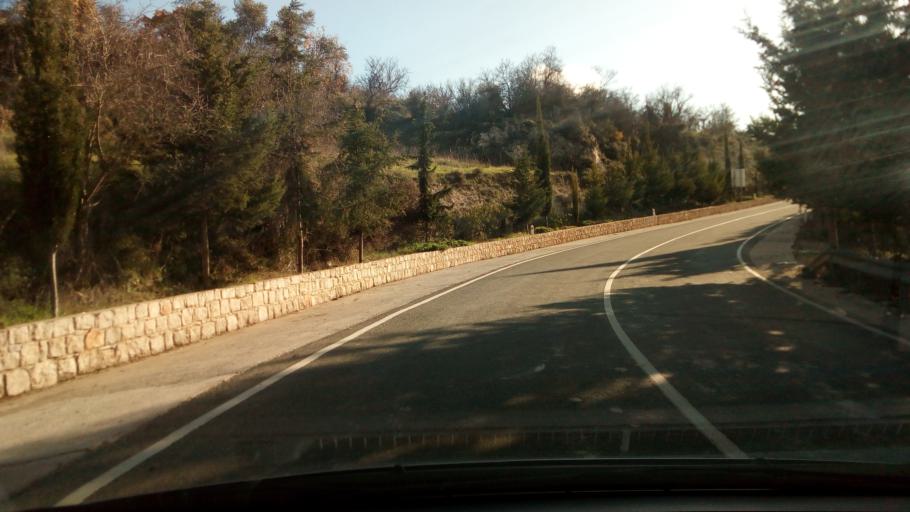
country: CY
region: Pafos
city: Tala
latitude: 34.9219
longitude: 32.5277
